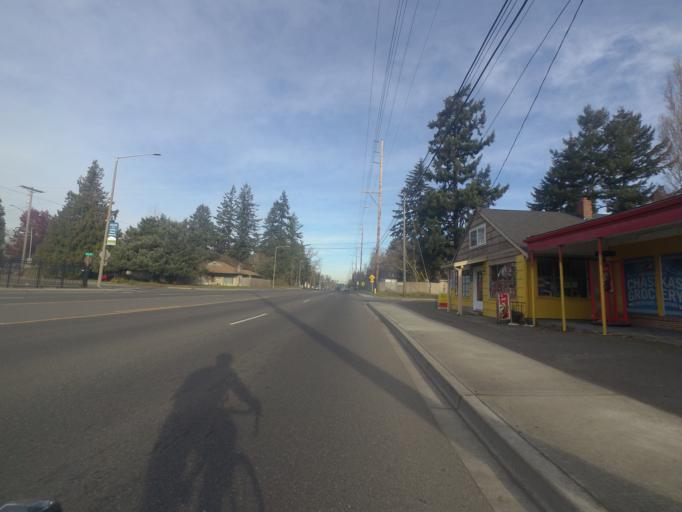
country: US
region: Washington
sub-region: Pierce County
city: Lakewood
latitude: 47.1774
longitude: -122.5180
